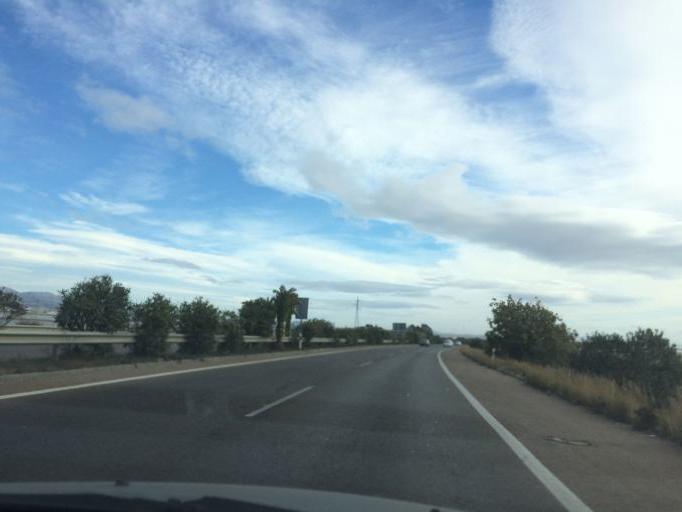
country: ES
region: Andalusia
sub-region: Provincia de Almeria
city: Almeria
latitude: 36.8454
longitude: -2.4157
